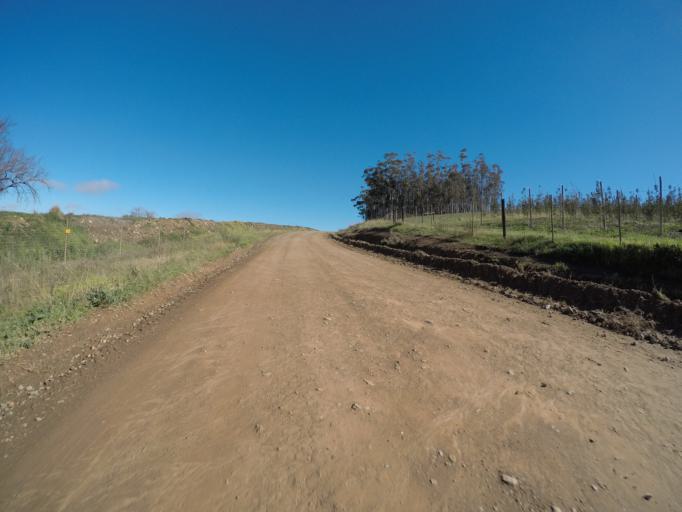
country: ZA
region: Western Cape
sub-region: Overberg District Municipality
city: Caledon
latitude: -34.0950
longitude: 19.6948
